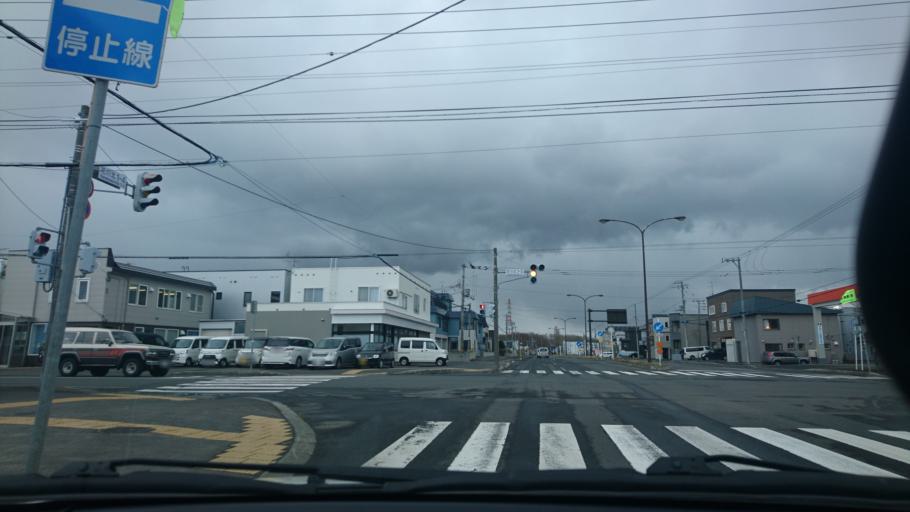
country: JP
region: Hokkaido
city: Sapporo
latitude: 43.1520
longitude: 141.3073
